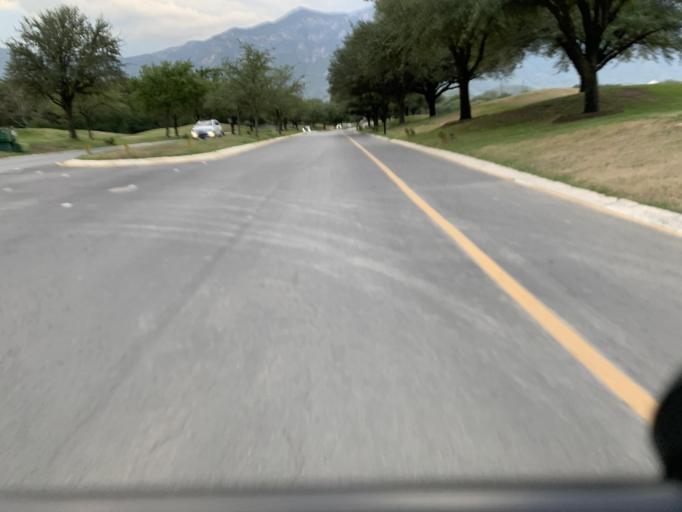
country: MX
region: Nuevo Leon
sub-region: Juarez
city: Bosques de San Pedro
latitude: 25.5185
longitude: -100.1939
